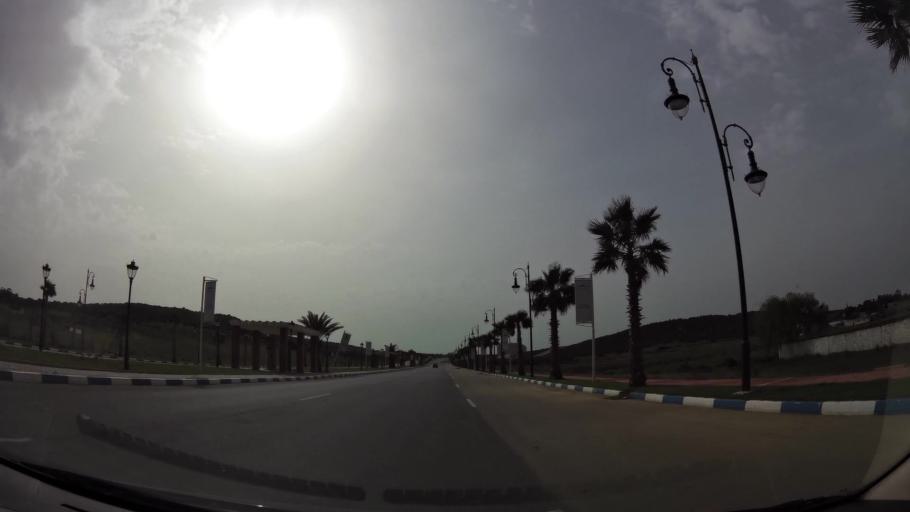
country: MA
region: Tanger-Tetouan
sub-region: Tanger-Assilah
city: Boukhalef
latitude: 35.6969
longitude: -5.9191
